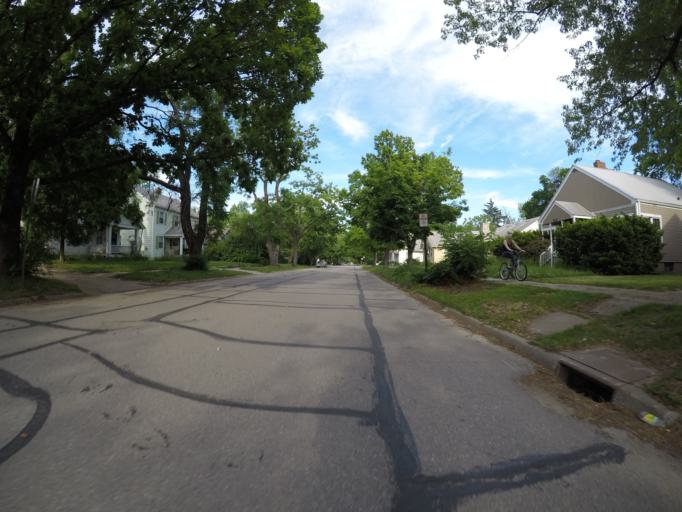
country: US
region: Kansas
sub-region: Riley County
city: Manhattan
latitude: 39.1909
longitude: -96.5708
